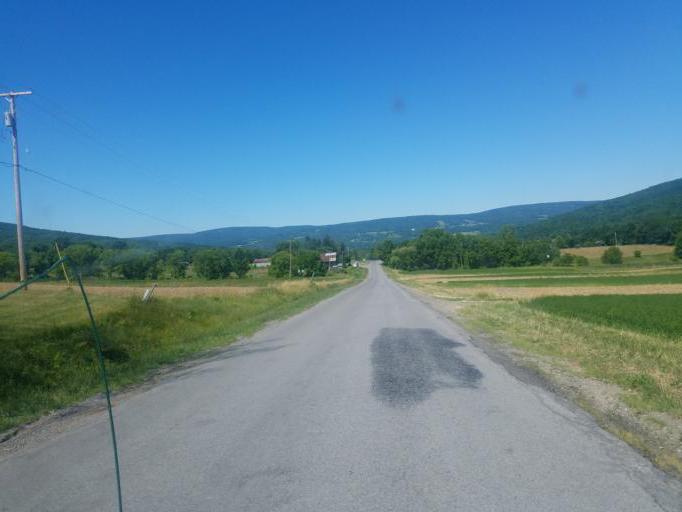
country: US
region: New York
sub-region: Ontario County
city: Canandaigua
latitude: 42.7256
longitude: -77.2891
